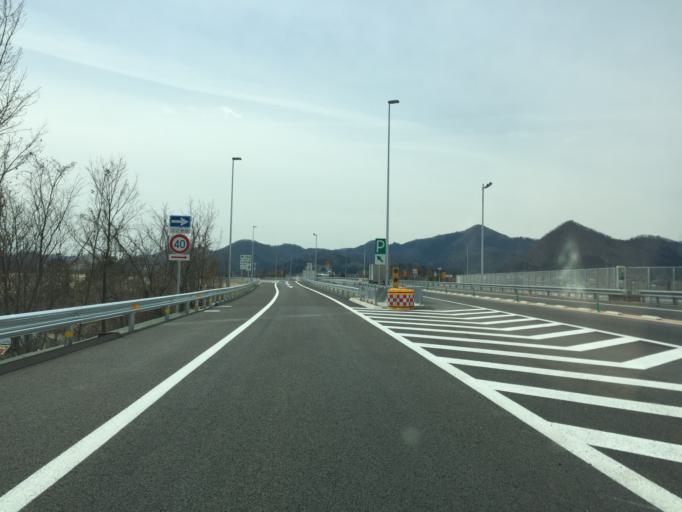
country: JP
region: Yamagata
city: Yamagata-shi
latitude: 38.2472
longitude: 140.2799
